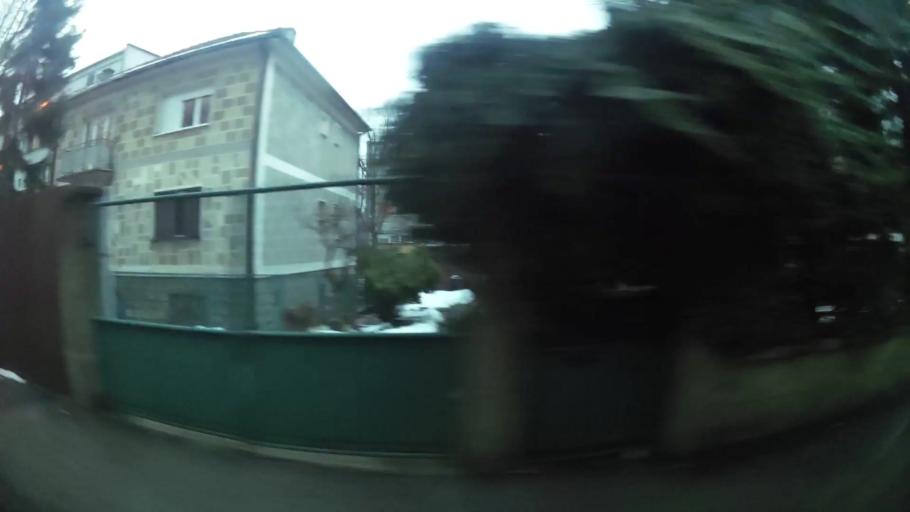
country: RS
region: Central Serbia
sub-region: Belgrade
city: Vozdovac
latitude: 44.7719
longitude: 20.4897
